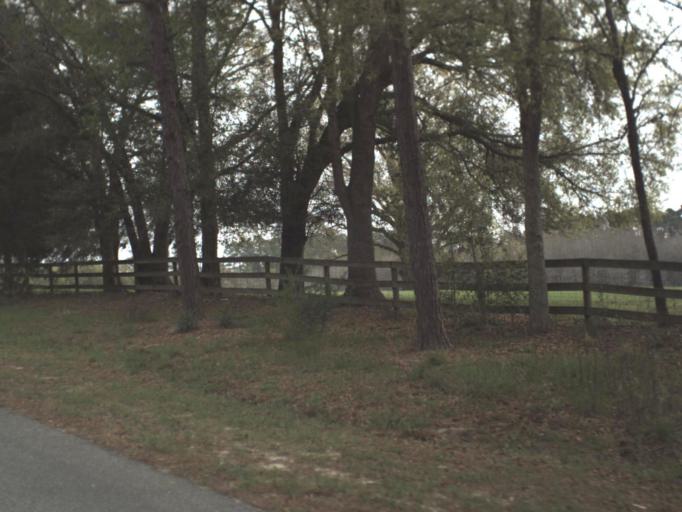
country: US
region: Florida
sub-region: Holmes County
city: Bonifay
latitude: 30.8672
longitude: -85.6656
